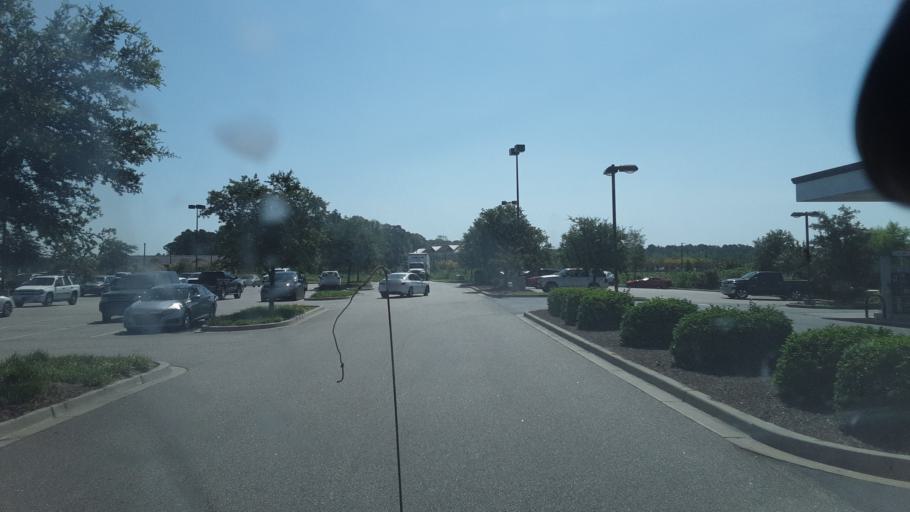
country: US
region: South Carolina
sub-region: Horry County
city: Myrtle Beach
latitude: 33.7591
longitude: -78.8561
